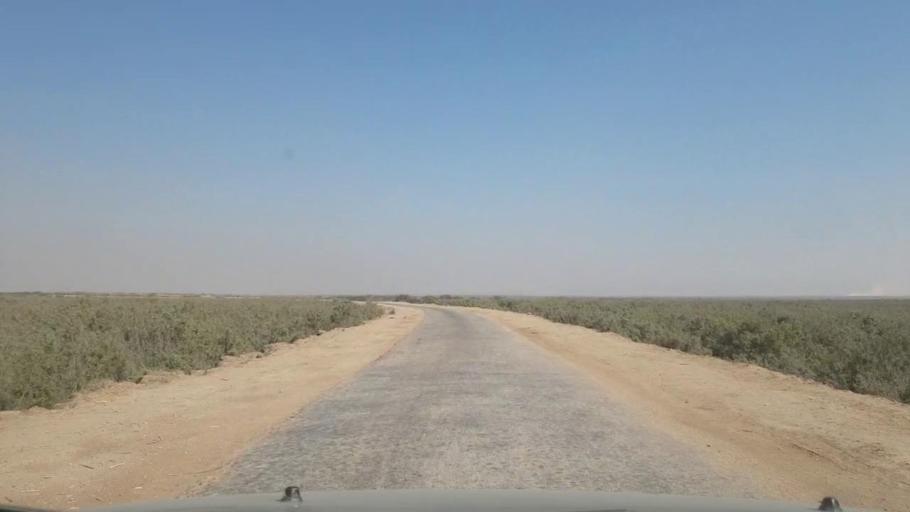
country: PK
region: Sindh
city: Thatta
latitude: 24.8223
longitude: 67.8923
